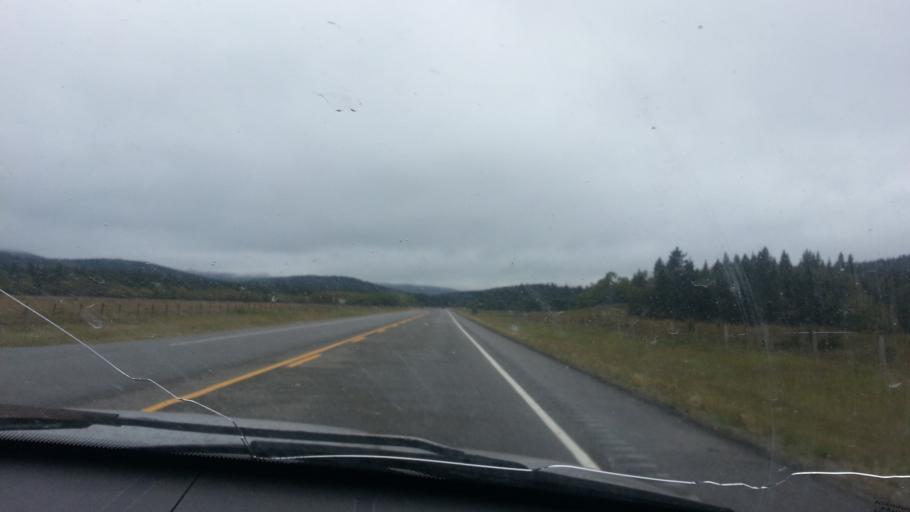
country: CA
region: Alberta
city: Cochrane
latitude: 51.0412
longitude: -114.7049
